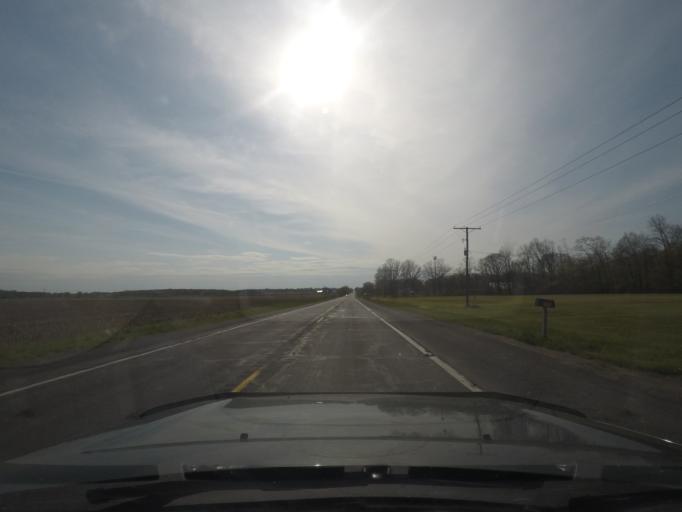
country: US
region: Michigan
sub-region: Berrien County
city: Three Oaks
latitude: 41.7986
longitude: -86.5786
